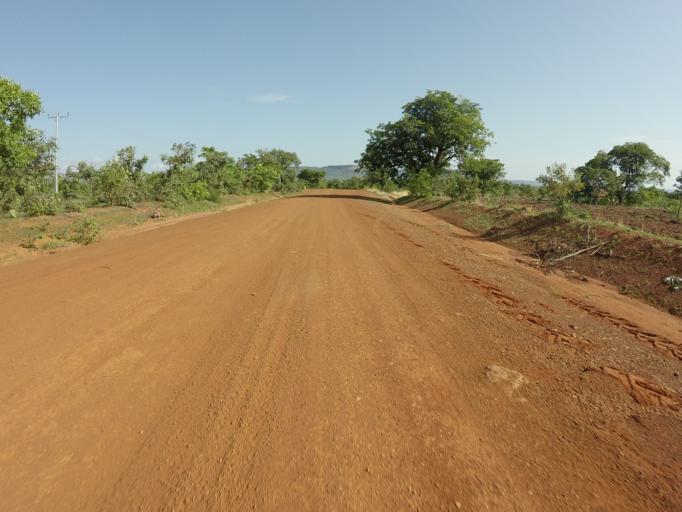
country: GH
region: Upper East
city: Bawku
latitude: 10.6917
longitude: -0.2158
